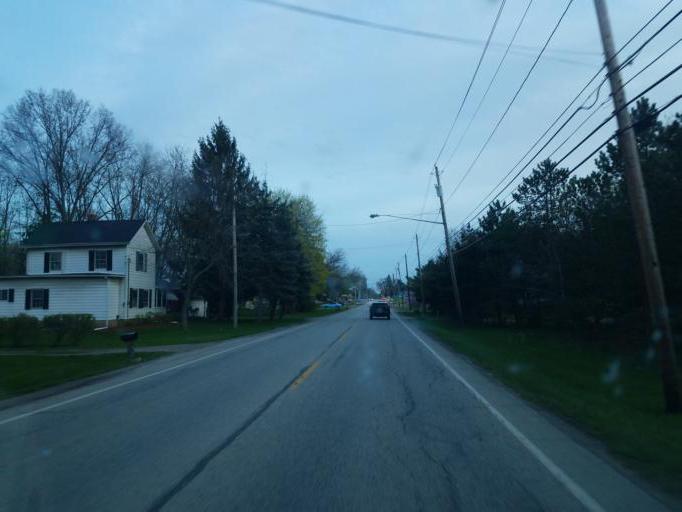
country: US
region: Ohio
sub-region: Lorain County
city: North Ridgeville
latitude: 41.3931
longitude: -82.0187
